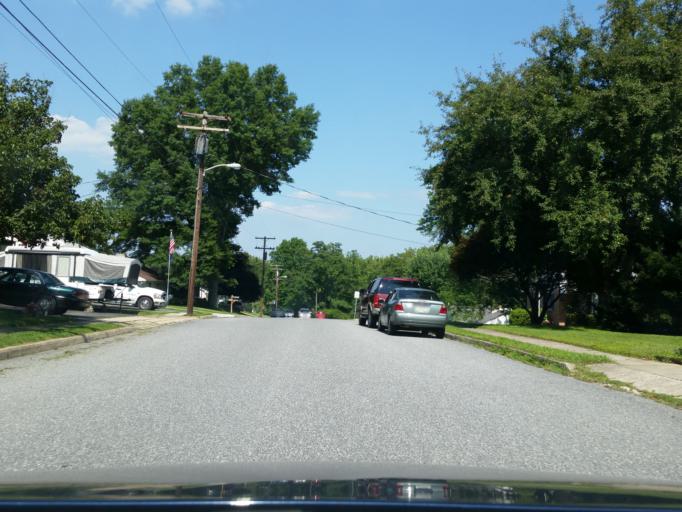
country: US
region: Pennsylvania
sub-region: York County
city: Hallam
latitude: 39.9987
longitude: -76.6141
